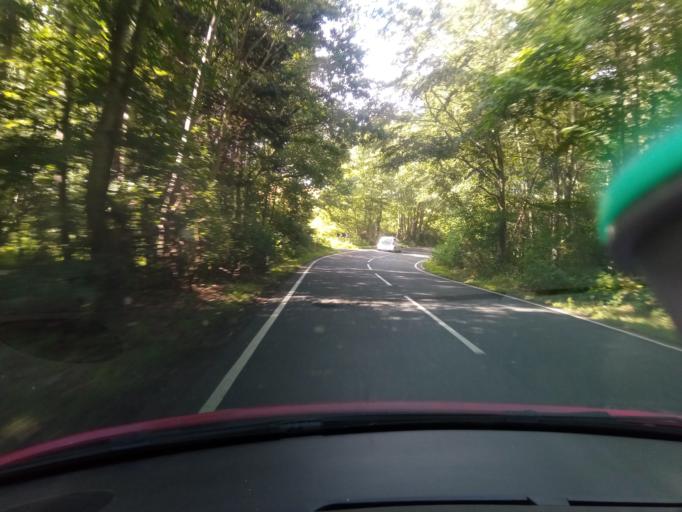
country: GB
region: Scotland
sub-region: The Scottish Borders
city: Jedburgh
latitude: 55.5723
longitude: -2.5305
